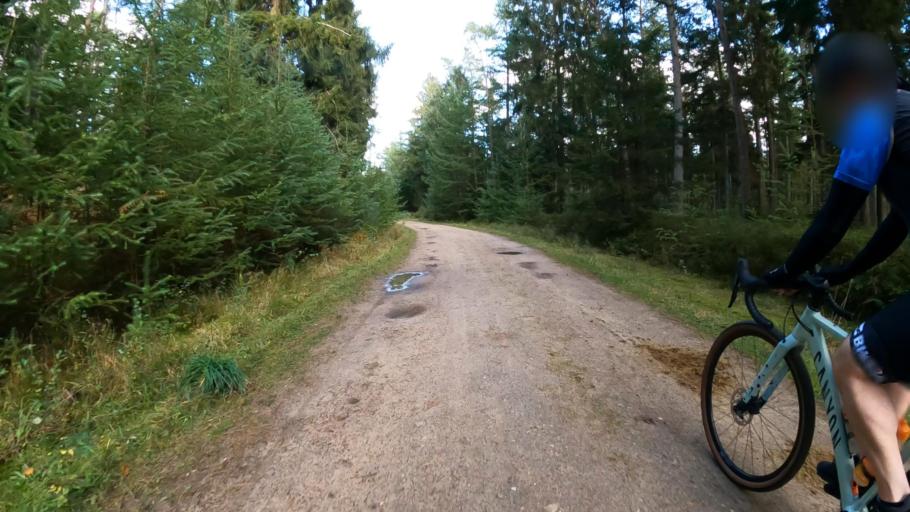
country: DE
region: Schleswig-Holstein
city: Hartenholm
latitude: 53.9320
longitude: 10.0788
